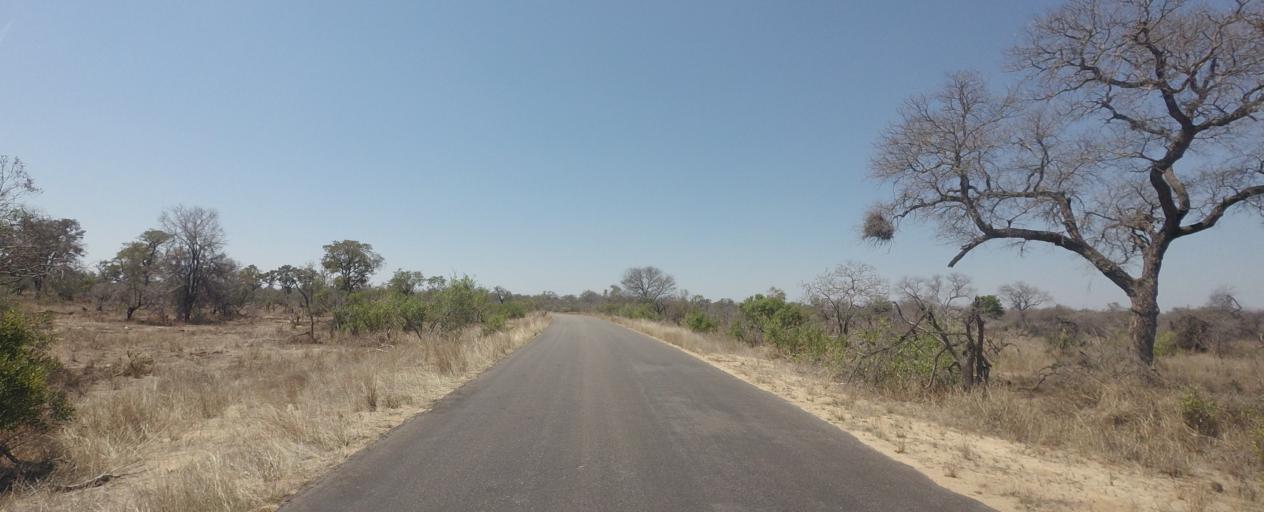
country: ZA
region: Limpopo
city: Thulamahashi
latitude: -24.4225
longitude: 31.5102
